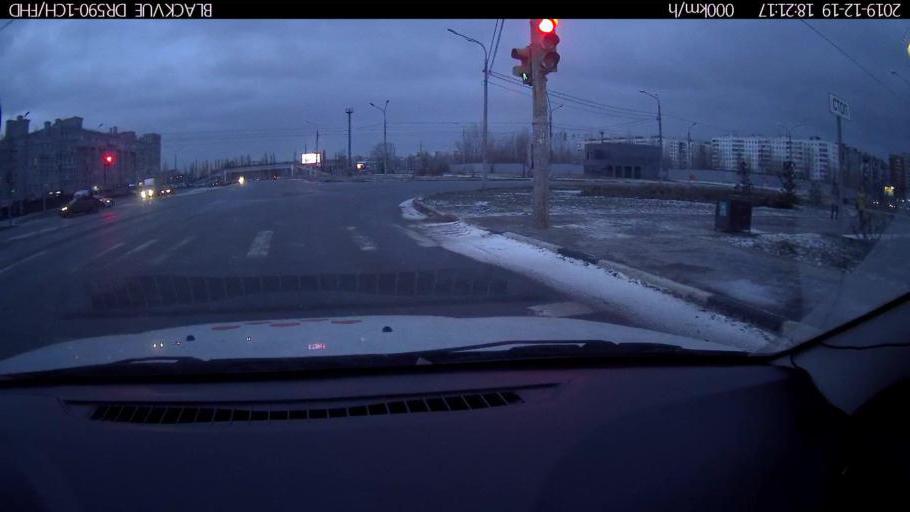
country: RU
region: Nizjnij Novgorod
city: Nizhniy Novgorod
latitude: 56.3319
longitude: 43.9517
